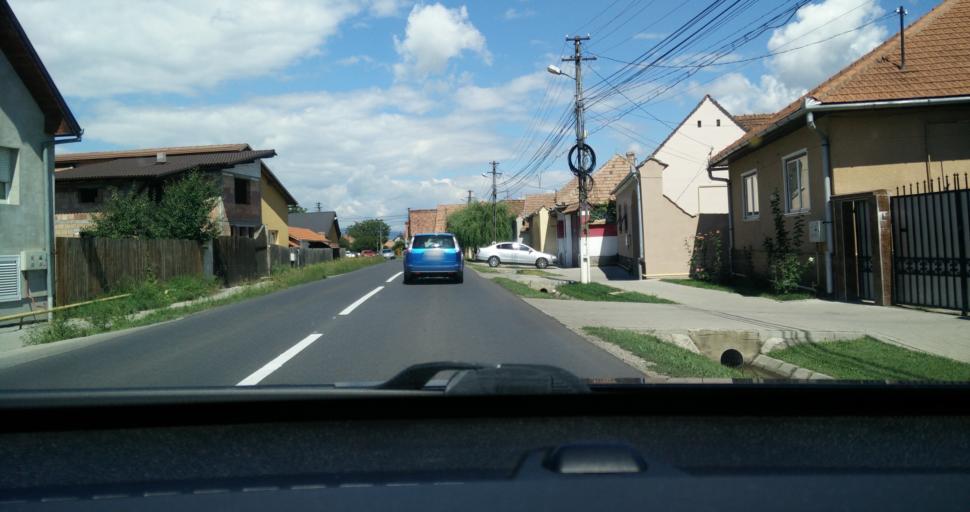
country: RO
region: Alba
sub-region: Municipiul Sebes
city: Petresti
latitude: 45.9271
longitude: 23.5610
